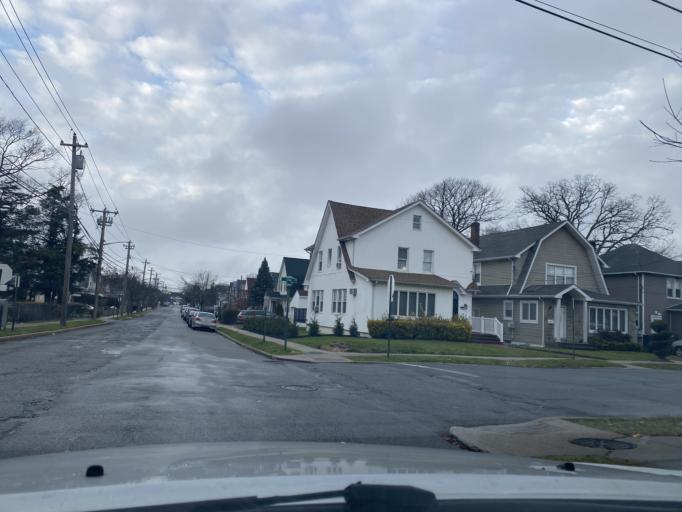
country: US
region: New York
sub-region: Nassau County
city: Cedarhurst
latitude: 40.6230
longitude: -73.7286
